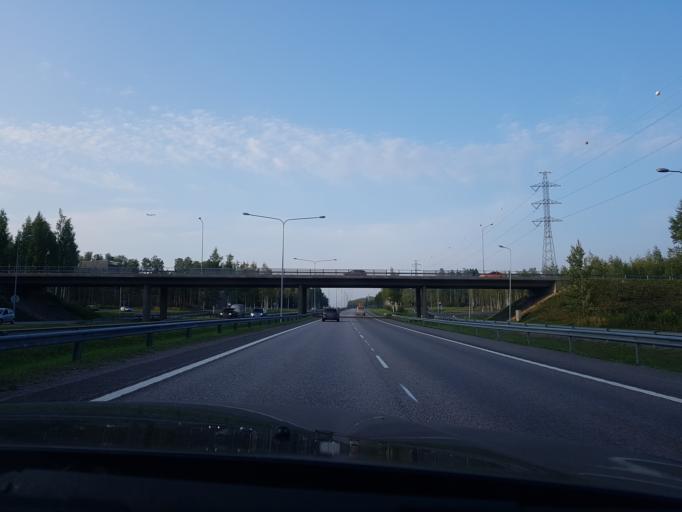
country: FI
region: Uusimaa
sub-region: Helsinki
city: Vantaa
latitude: 60.3222
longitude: 24.9972
